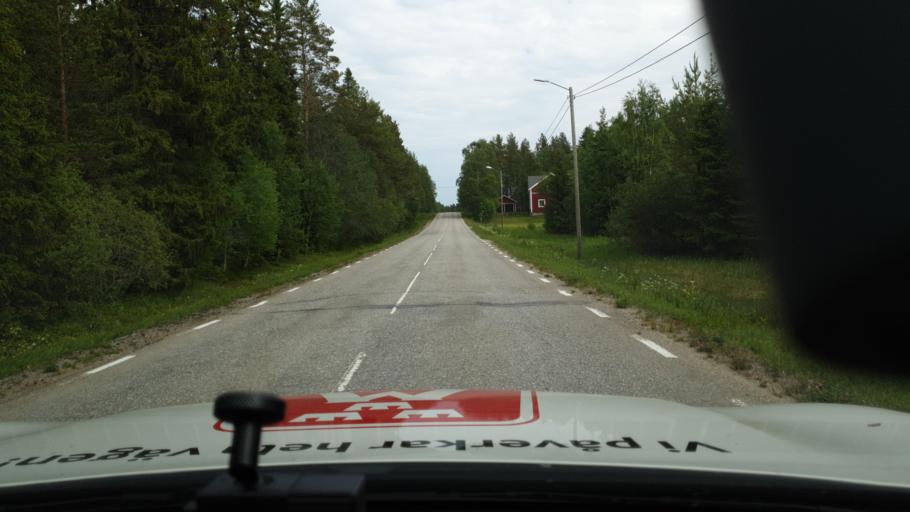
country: SE
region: Vaesterbotten
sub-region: Umea Kommun
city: Hoernefors
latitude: 63.5635
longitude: 19.7705
